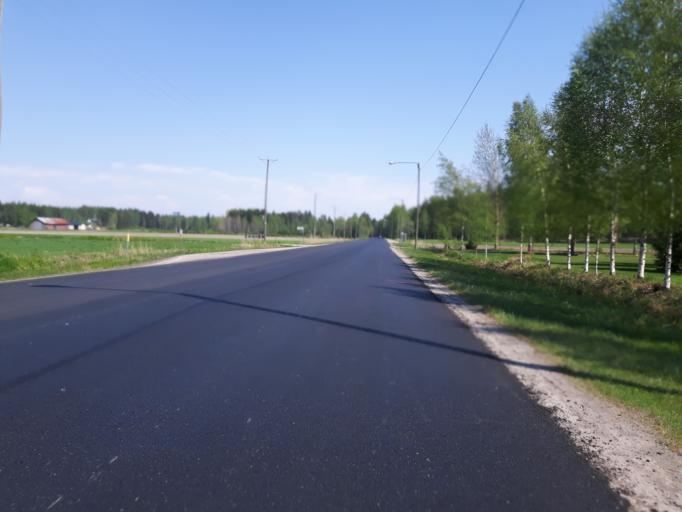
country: FI
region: Uusimaa
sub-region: Helsinki
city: Pornainen
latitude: 60.3327
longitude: 25.4517
